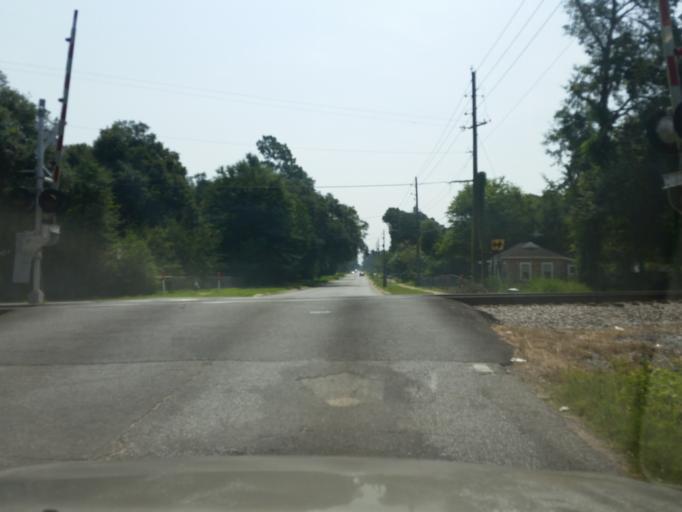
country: US
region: Florida
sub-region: Escambia County
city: Ensley
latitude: 30.5194
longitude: -87.2630
